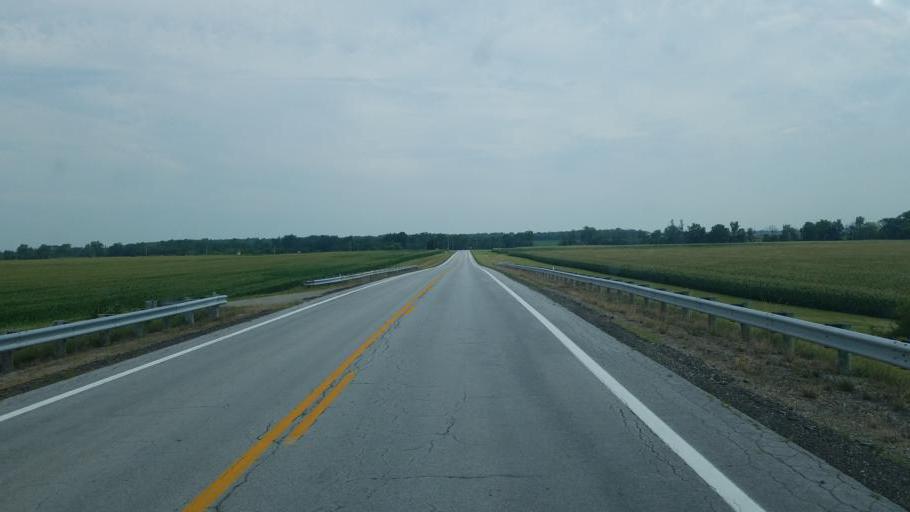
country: US
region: Ohio
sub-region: Madison County
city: Choctaw Lake
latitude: 39.9424
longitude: -83.4486
